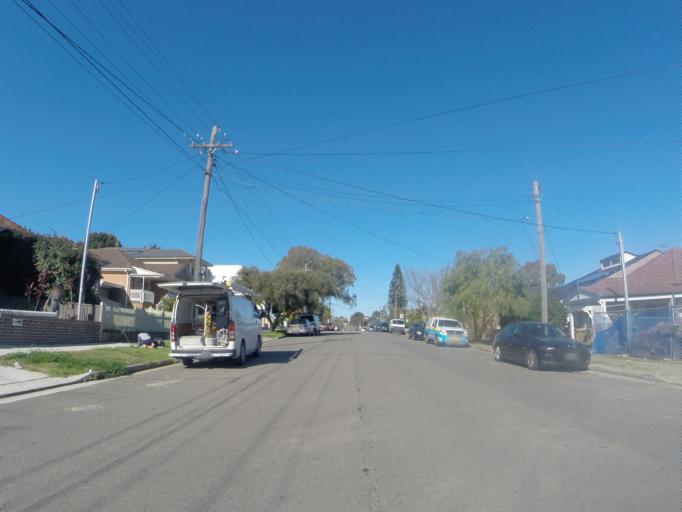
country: AU
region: New South Wales
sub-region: Hurstville
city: Earlwood
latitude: -33.9532
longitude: 151.0899
